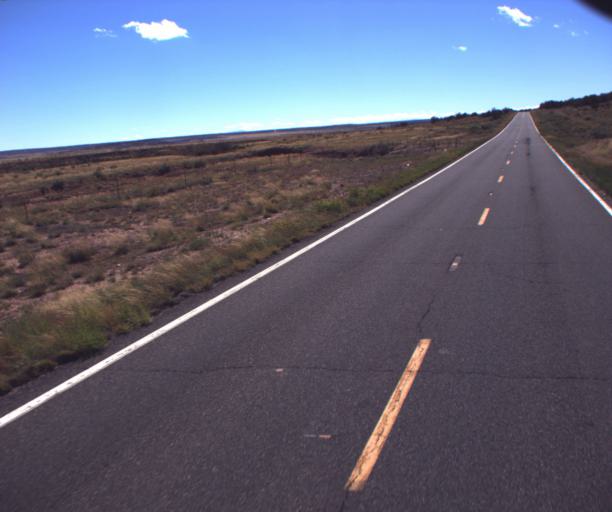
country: US
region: Arizona
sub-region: Apache County
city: Saint Johns
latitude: 34.7410
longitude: -109.2495
